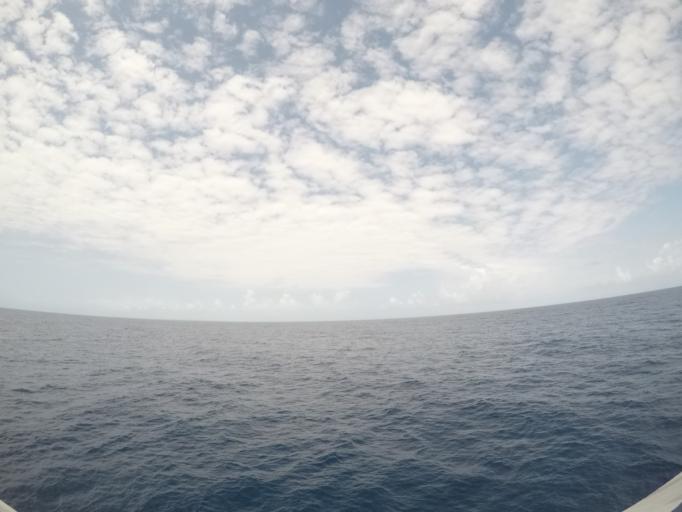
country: TZ
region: Zanzibar North
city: Nungwi
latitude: -5.5887
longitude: 39.3512
